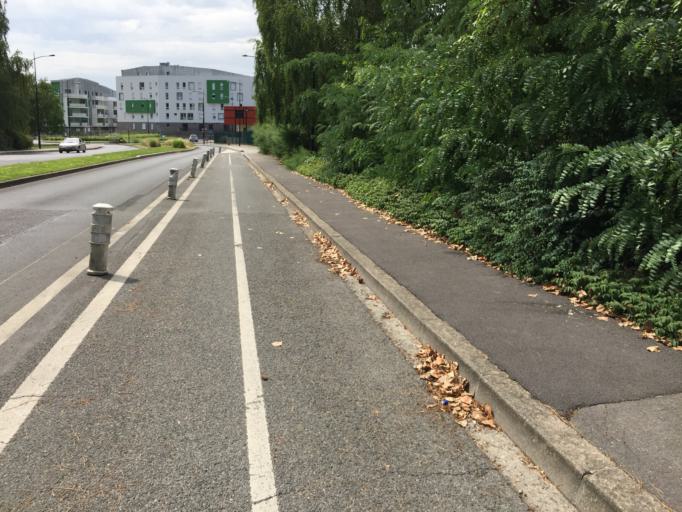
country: FR
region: Ile-de-France
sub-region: Departement de Seine-et-Marne
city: Meaux
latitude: 48.9531
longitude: 2.9006
